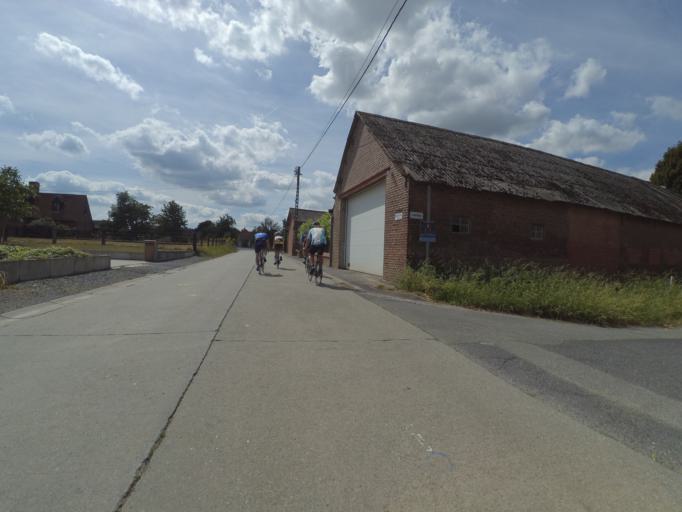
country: BE
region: Flanders
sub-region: Provincie Oost-Vlaanderen
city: Zingem
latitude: 50.8393
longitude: 3.7044
